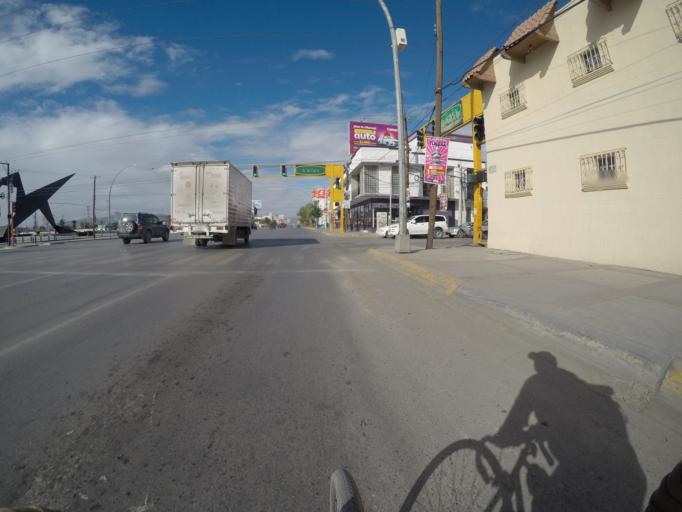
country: MX
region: Chihuahua
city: Ciudad Juarez
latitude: 31.7388
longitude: -106.4330
